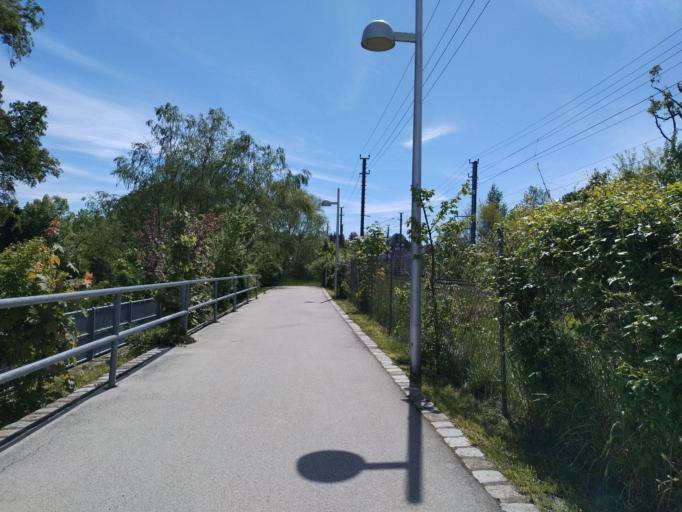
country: AT
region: Lower Austria
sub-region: Politischer Bezirk Wien-Umgebung
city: Purkersdorf
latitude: 48.2095
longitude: 16.2295
